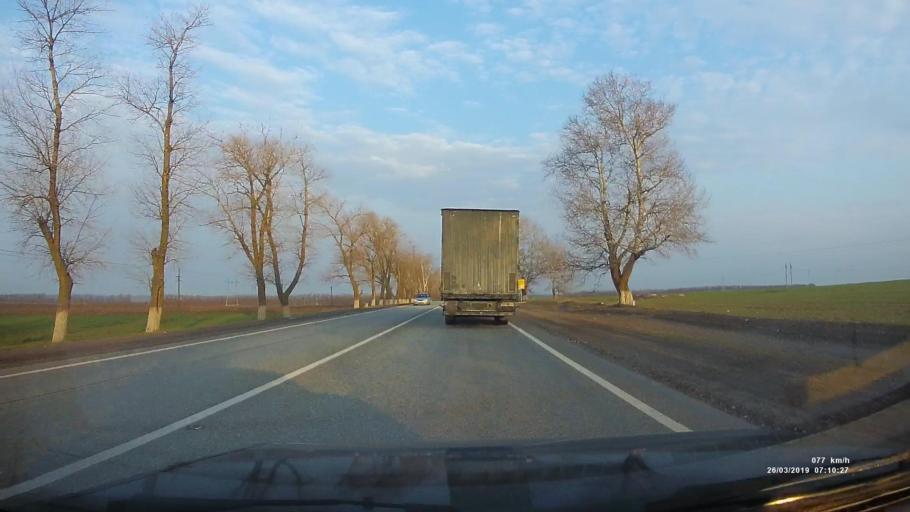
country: RU
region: Rostov
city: Primorka
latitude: 47.3193
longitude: 39.0917
